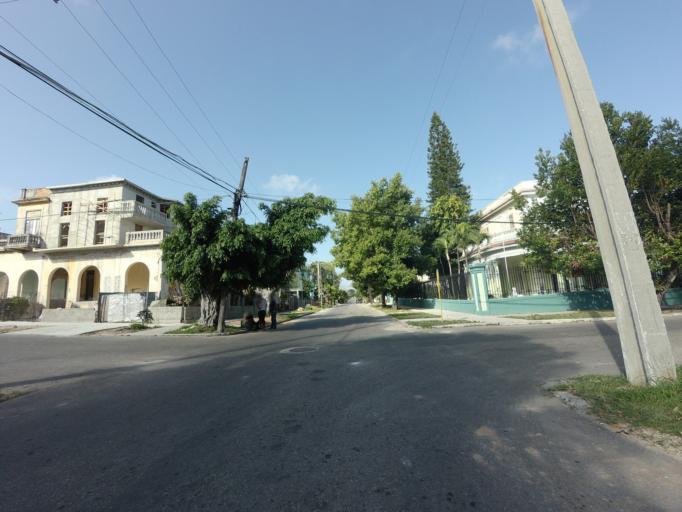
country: CU
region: La Habana
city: Havana
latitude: 23.1318
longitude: -82.3900
